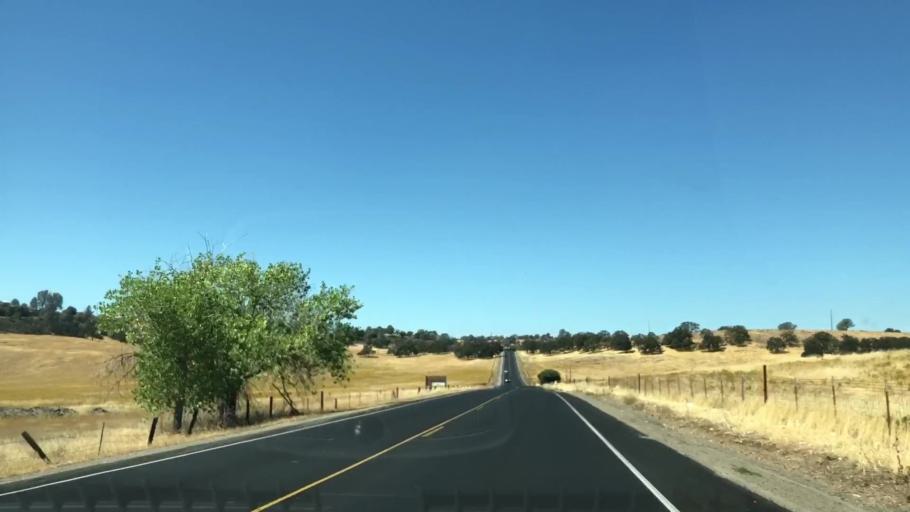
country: US
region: California
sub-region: Tuolumne County
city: Jamestown
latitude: 37.8801
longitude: -120.4666
